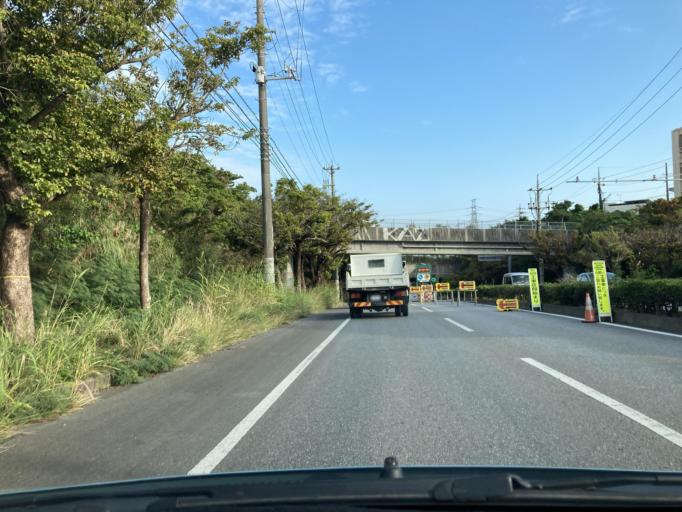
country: JP
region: Okinawa
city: Gushikawa
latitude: 26.3465
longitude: 127.8356
